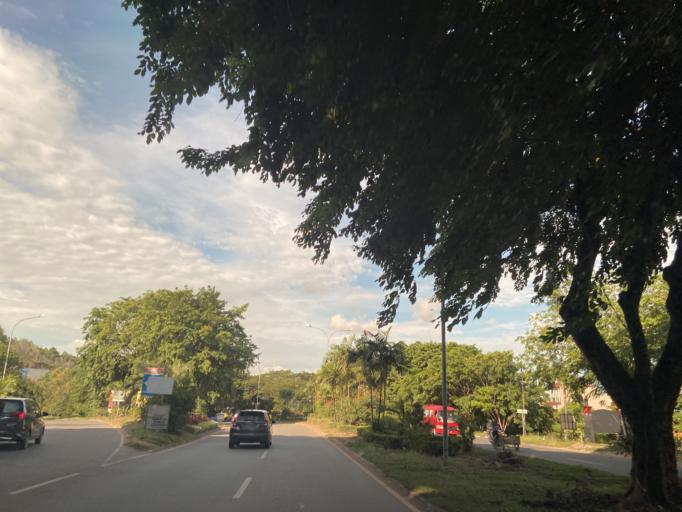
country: SG
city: Singapore
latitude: 1.1225
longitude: 104.0161
